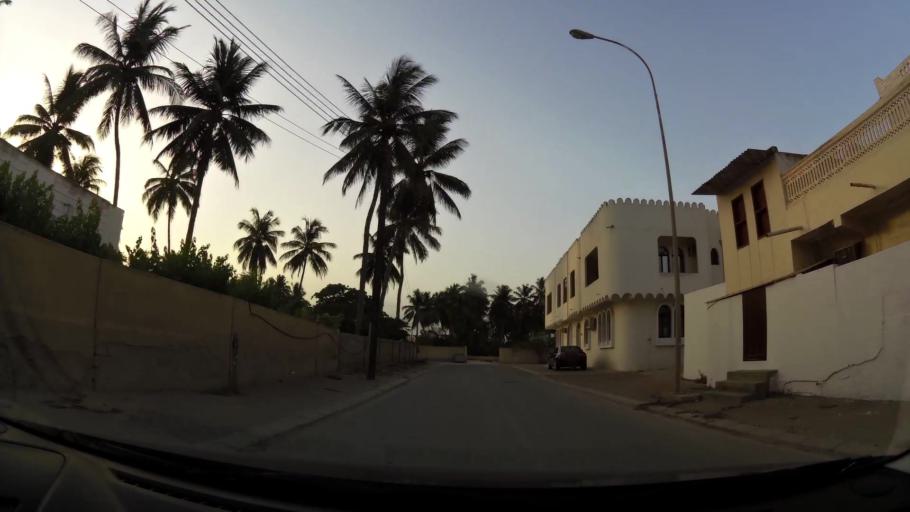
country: OM
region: Zufar
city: Salalah
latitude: 17.0174
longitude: 54.1197
